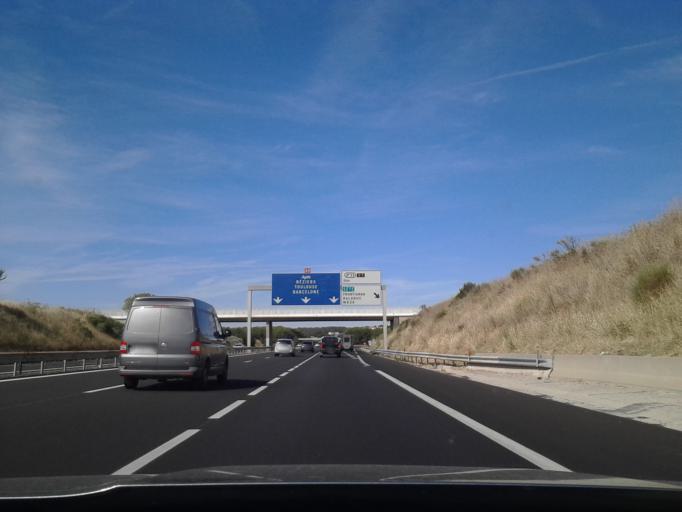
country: FR
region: Languedoc-Roussillon
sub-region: Departement de l'Herault
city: Poussan
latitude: 43.4832
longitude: 3.6901
